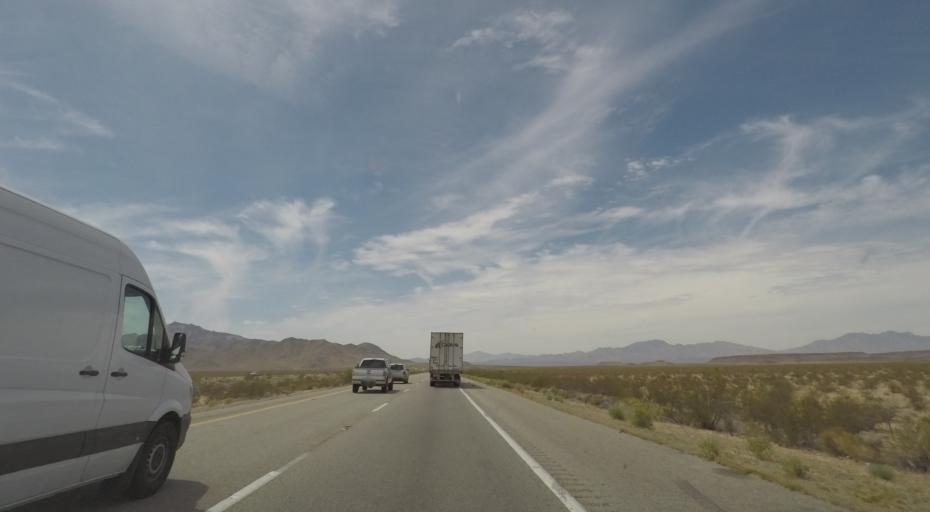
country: US
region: California
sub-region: San Bernardino County
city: Needles
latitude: 34.8035
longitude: -115.2929
